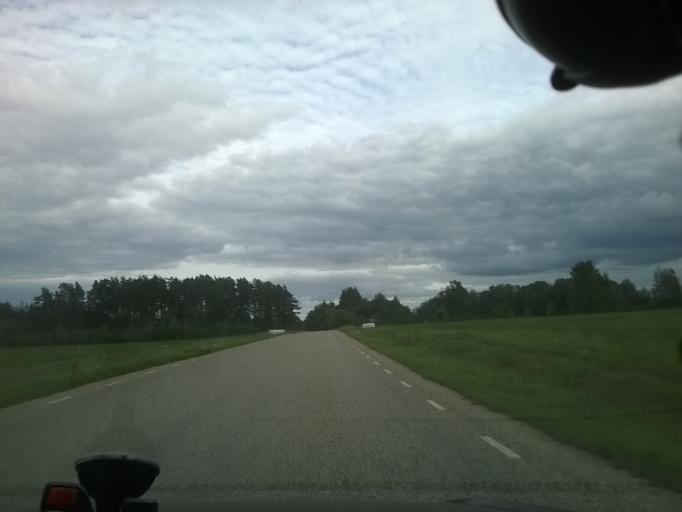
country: EE
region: Vorumaa
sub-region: Voru linn
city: Voru
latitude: 57.7493
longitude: 26.9682
